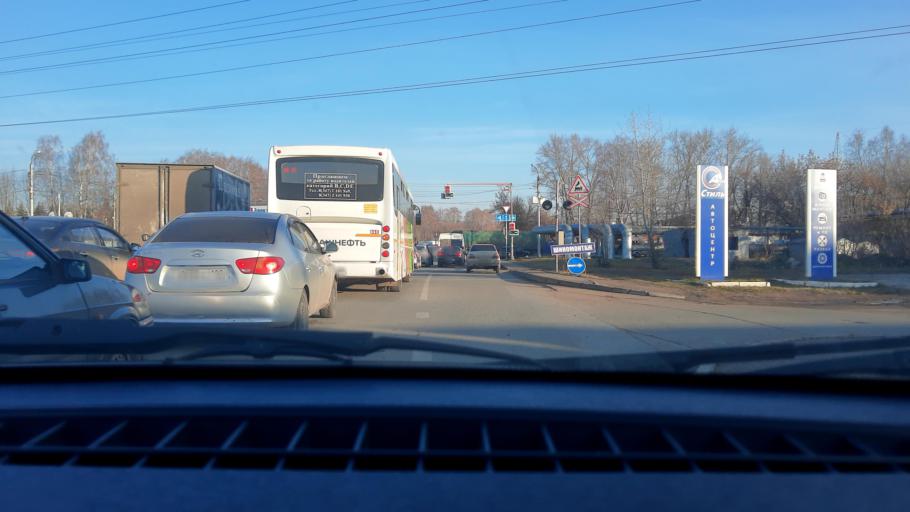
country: RU
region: Bashkortostan
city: Ufa
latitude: 54.7971
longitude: 56.0769
